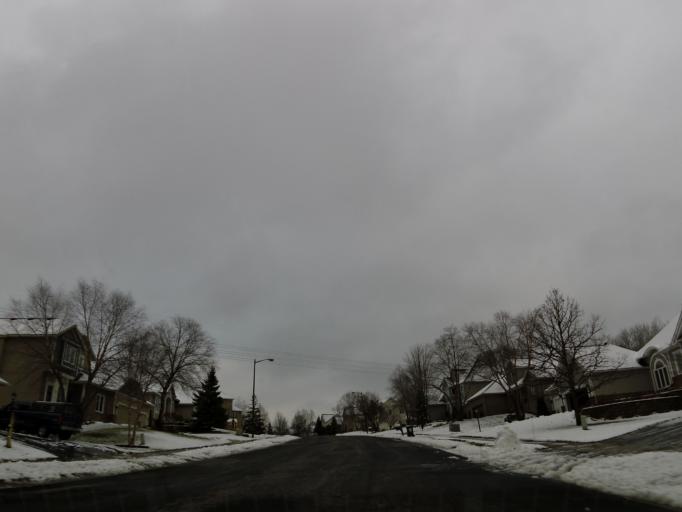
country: US
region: Minnesota
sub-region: Dakota County
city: Apple Valley
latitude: 44.7133
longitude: -93.2517
